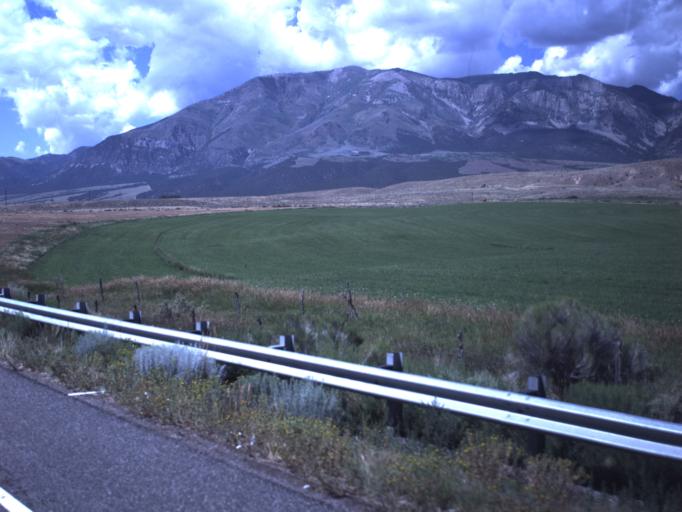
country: US
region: Utah
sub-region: Piute County
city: Junction
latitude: 38.4339
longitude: -112.2311
